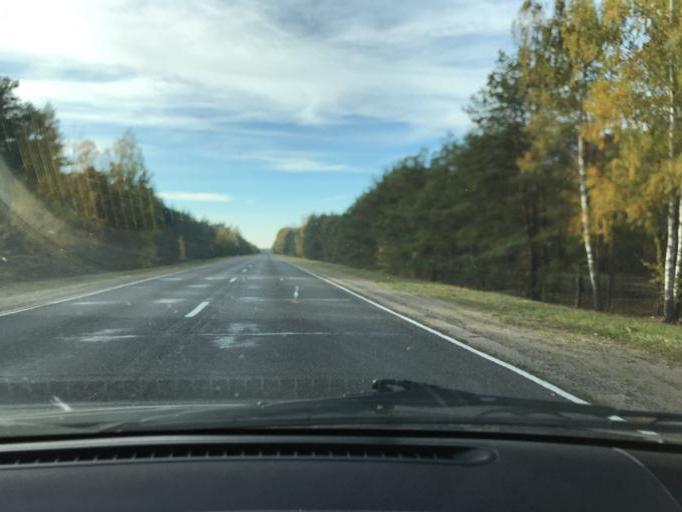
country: BY
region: Brest
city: Ivanava
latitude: 52.1554
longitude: 25.7857
